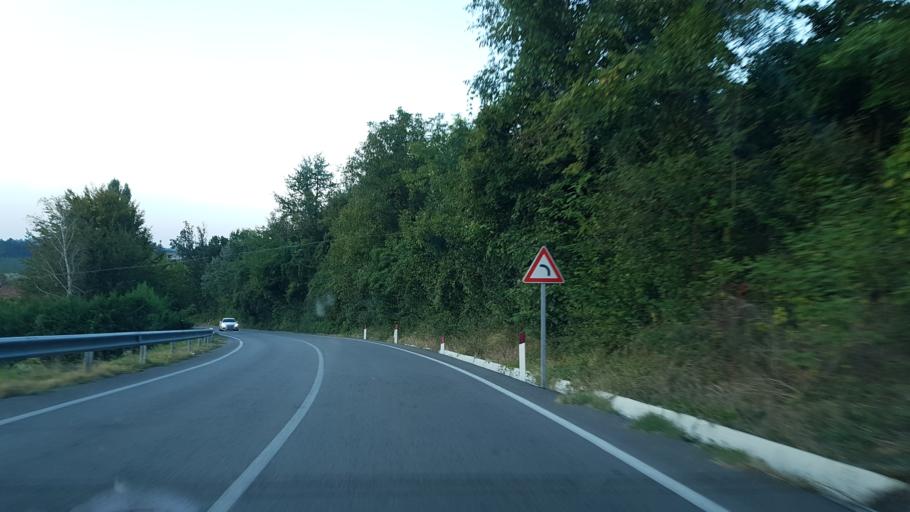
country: IT
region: Piedmont
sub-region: Provincia di Cuneo
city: Novello
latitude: 44.5872
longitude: 7.9089
